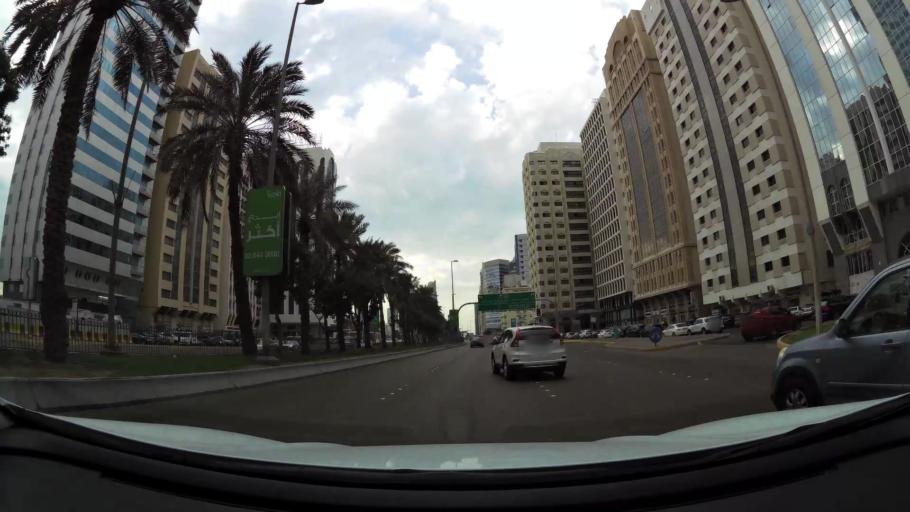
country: AE
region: Abu Dhabi
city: Abu Dhabi
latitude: 24.4734
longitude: 54.3678
